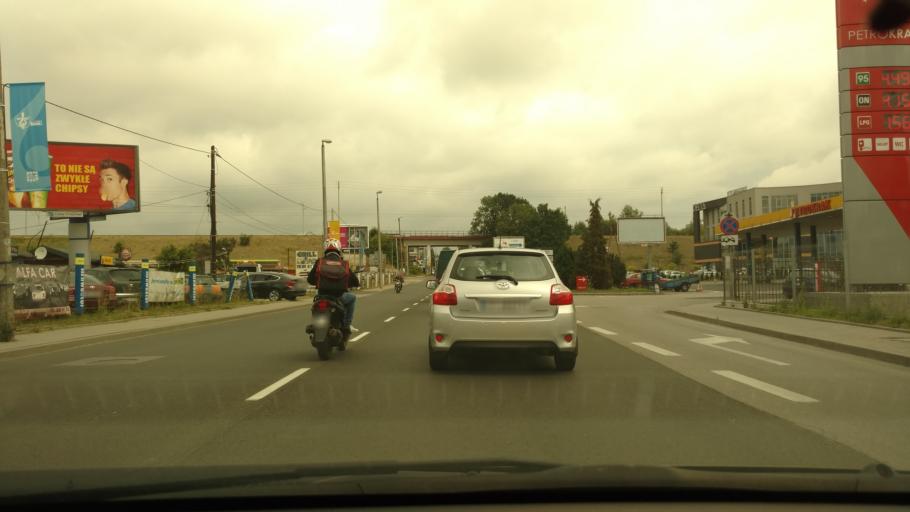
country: PL
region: Lesser Poland Voivodeship
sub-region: Krakow
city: Krakow
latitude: 50.0947
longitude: 19.9613
